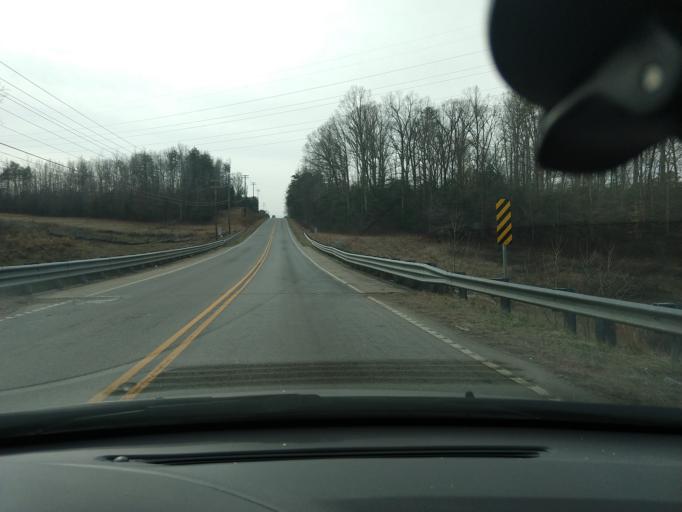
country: US
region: South Carolina
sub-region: Spartanburg County
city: Spartanburg
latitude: 34.9985
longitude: -81.8765
